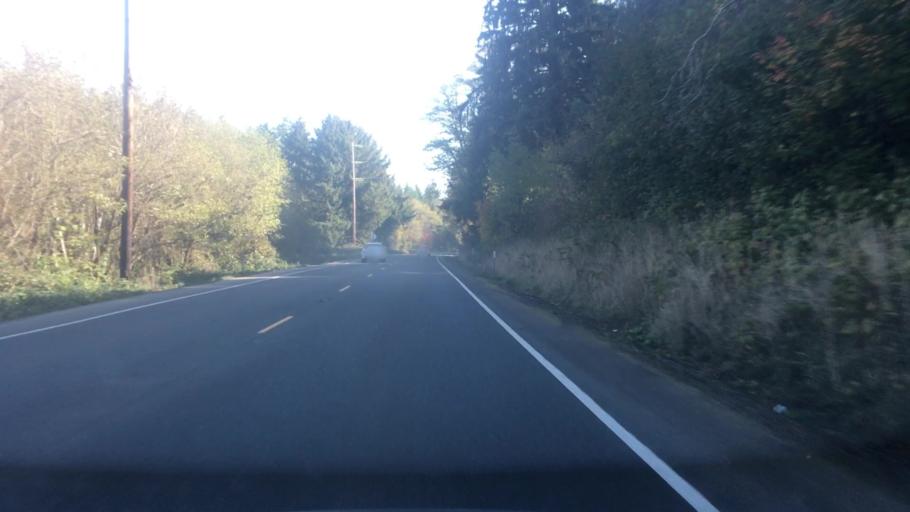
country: US
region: Oregon
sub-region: Lincoln County
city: Rose Lodge
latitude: 45.0126
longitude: -123.9286
